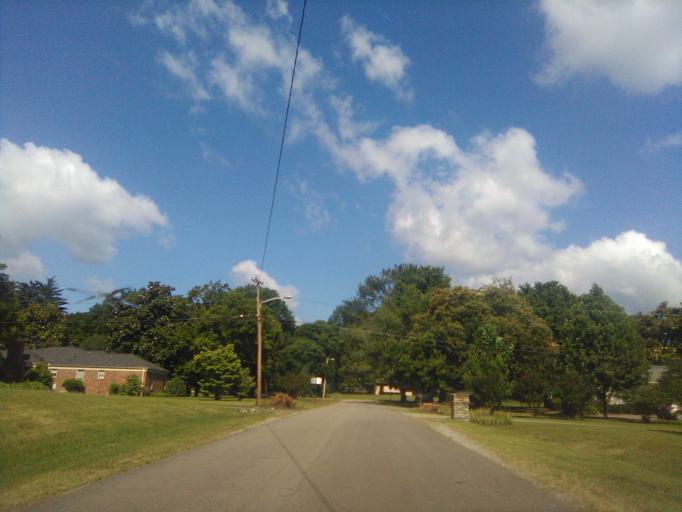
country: US
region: Tennessee
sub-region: Davidson County
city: Belle Meade
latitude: 36.1144
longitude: -86.8675
